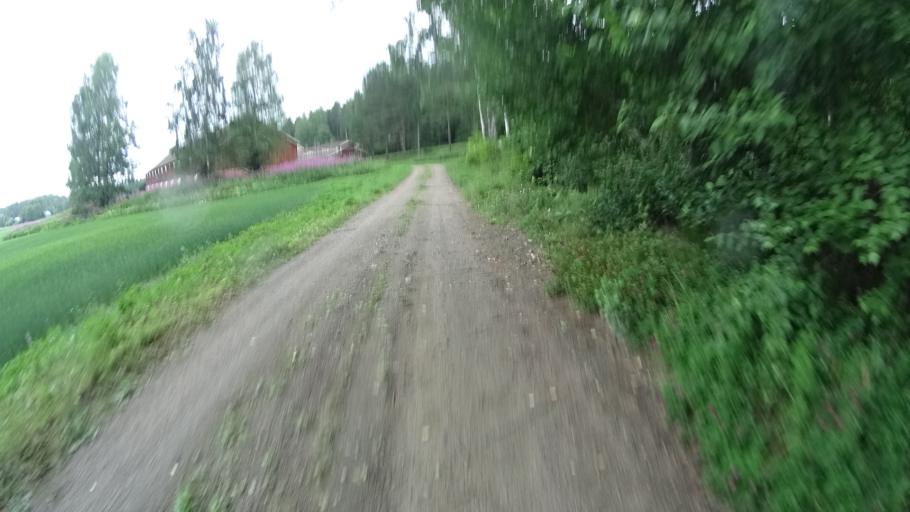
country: FI
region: Uusimaa
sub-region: Helsinki
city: Karkkila
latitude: 60.5690
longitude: 24.3230
